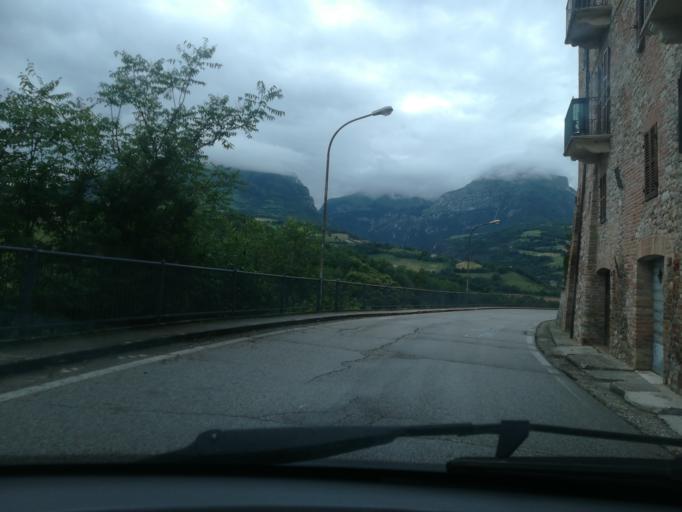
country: IT
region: The Marches
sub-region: Province of Fermo
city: Montefortino
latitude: 42.9418
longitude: 13.3419
